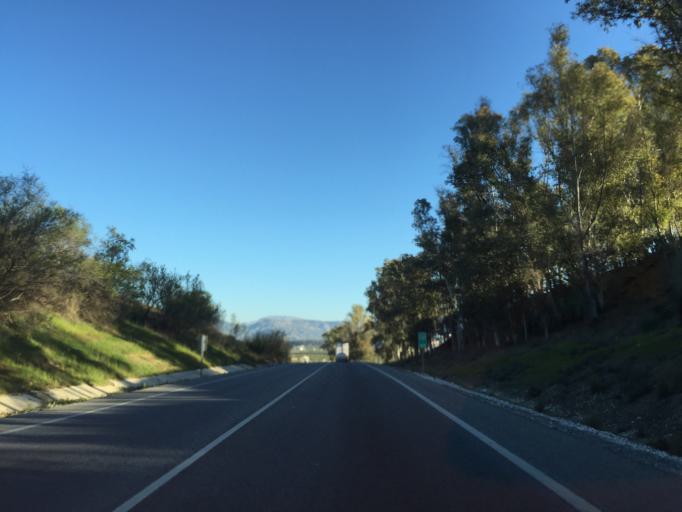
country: ES
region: Andalusia
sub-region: Provincia de Malaga
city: Pizarra
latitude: 36.7304
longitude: -4.7091
